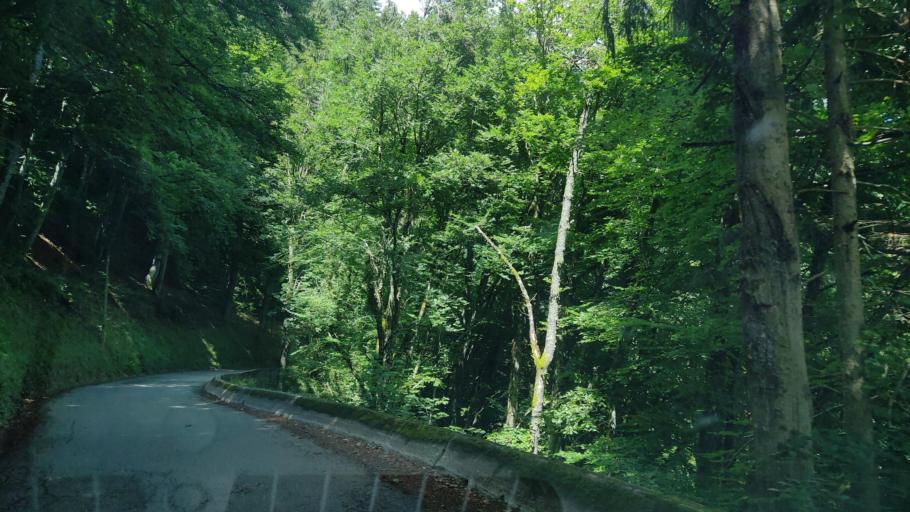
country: FR
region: Rhone-Alpes
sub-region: Departement de la Savoie
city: Beaufort
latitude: 45.7300
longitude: 6.5248
